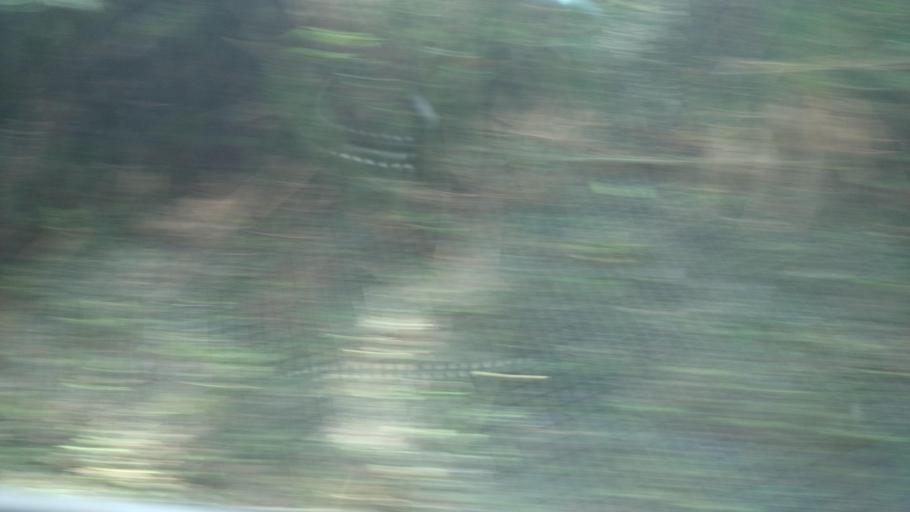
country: TW
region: Taiwan
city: Daxi
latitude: 24.9094
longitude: 121.4042
